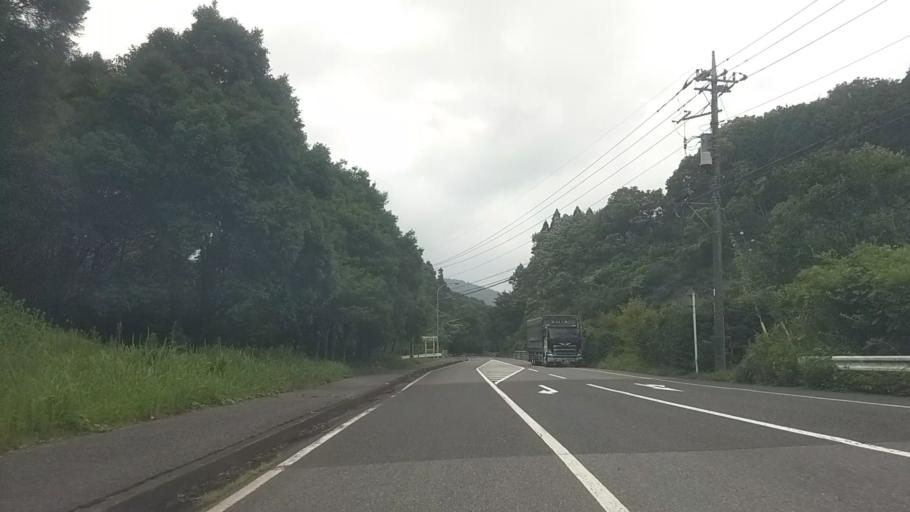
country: JP
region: Chiba
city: Kawaguchi
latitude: 35.2408
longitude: 140.0353
